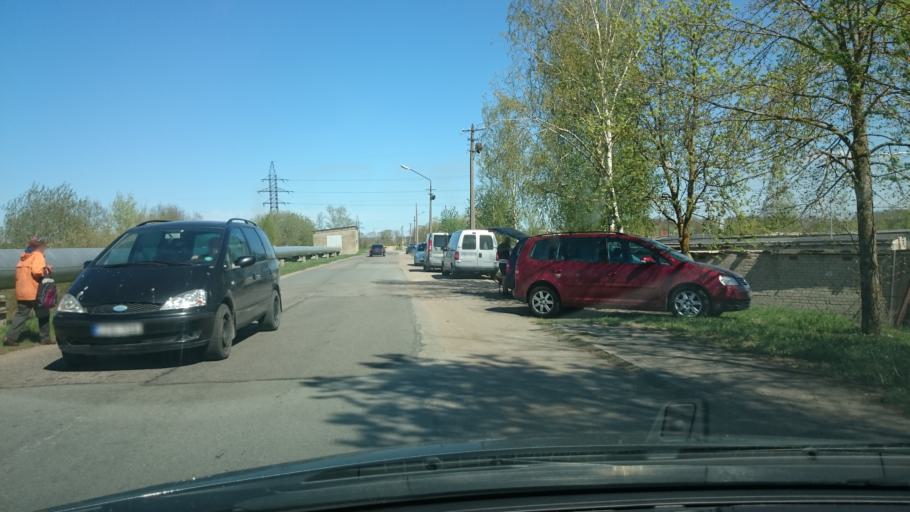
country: EE
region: Ida-Virumaa
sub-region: Narva linn
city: Narva
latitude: 59.3521
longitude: 28.1780
